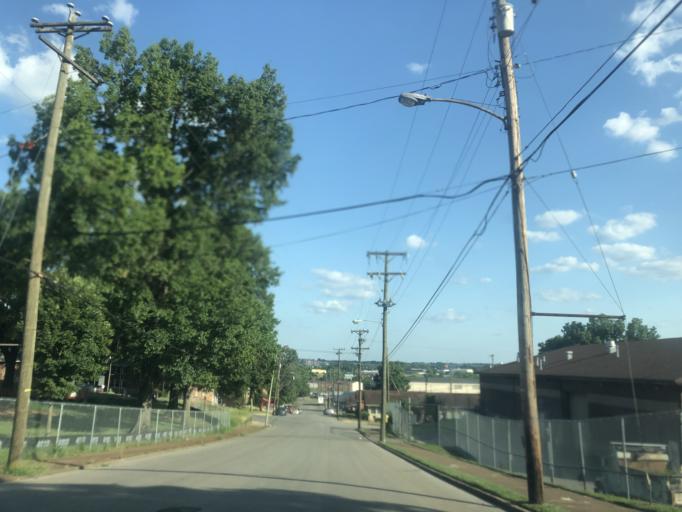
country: US
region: Tennessee
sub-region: Davidson County
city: Nashville
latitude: 36.1654
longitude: -86.7557
